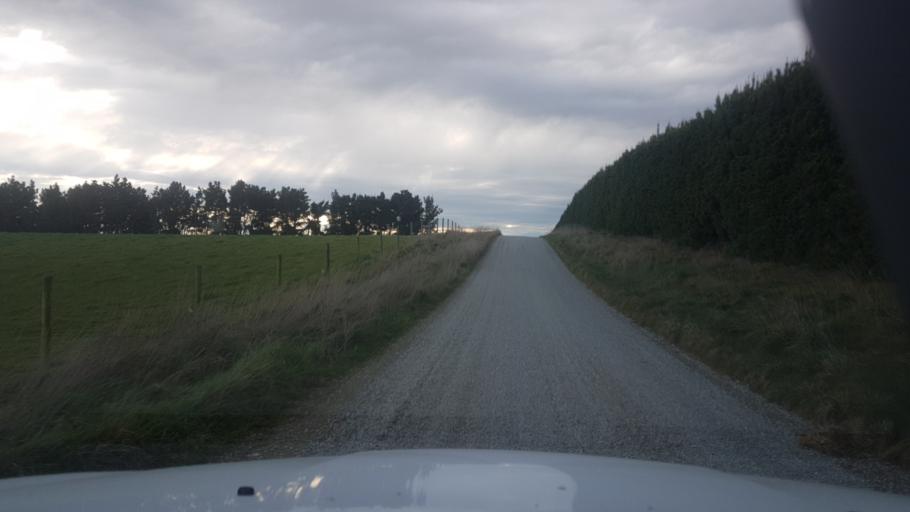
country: NZ
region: Canterbury
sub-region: Timaru District
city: Pleasant Point
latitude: -44.3416
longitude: 171.1421
